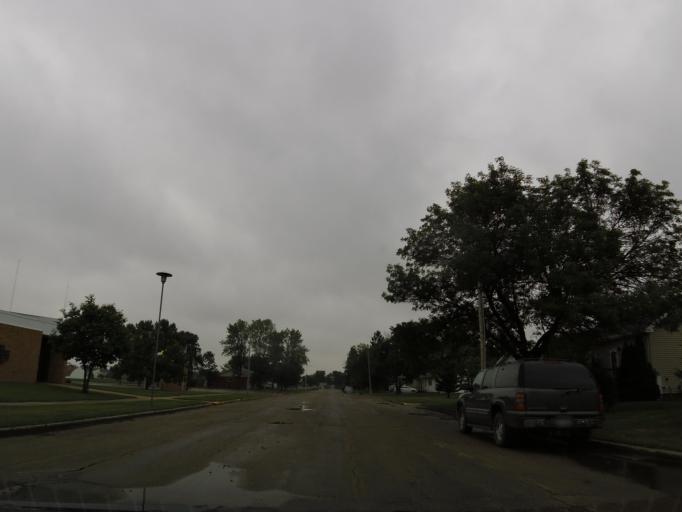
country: US
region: Minnesota
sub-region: Marshall County
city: Warren
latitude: 48.1974
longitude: -96.7622
